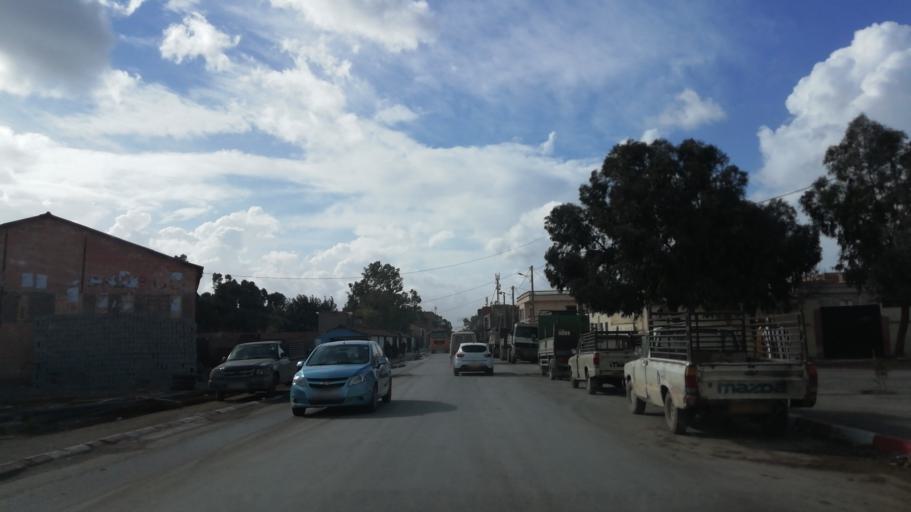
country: DZ
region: Oran
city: Sidi ech Chahmi
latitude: 35.6514
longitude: -0.5684
